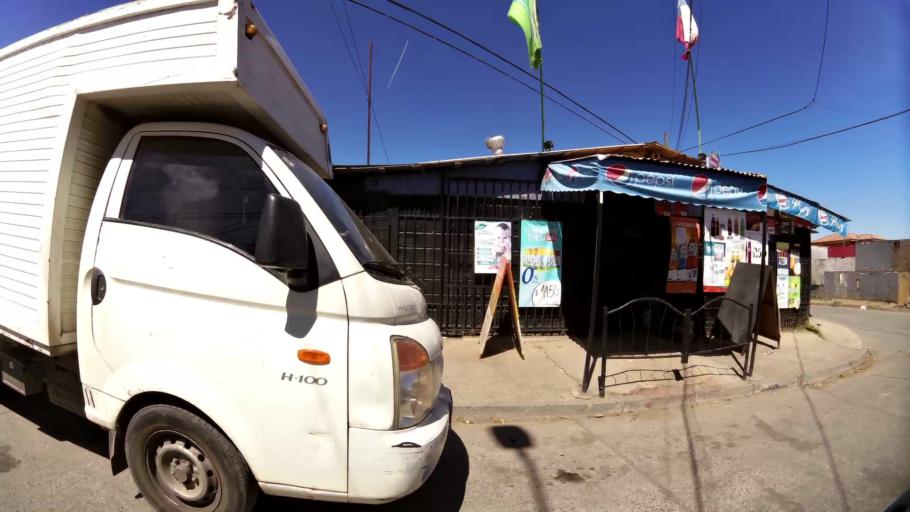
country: CL
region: O'Higgins
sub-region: Provincia de Cachapoal
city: Rancagua
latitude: -34.1684
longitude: -70.7141
